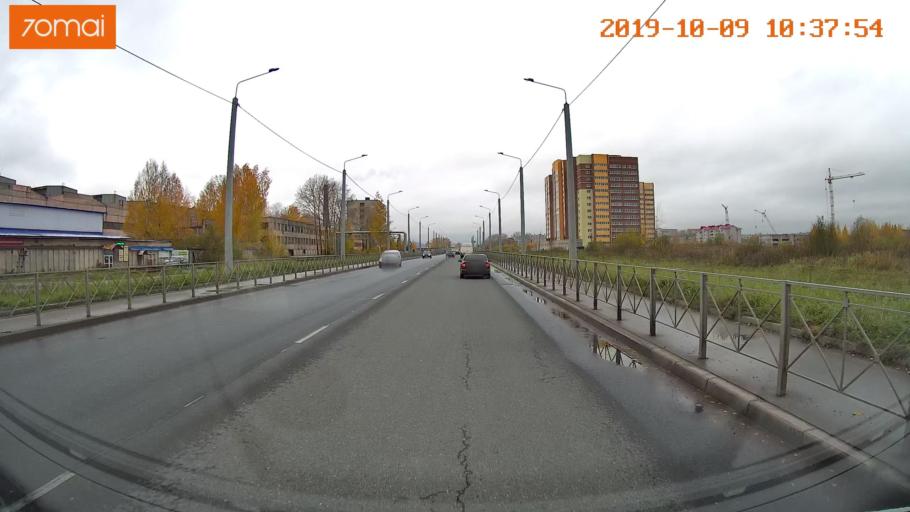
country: RU
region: Vologda
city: Vologda
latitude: 59.2357
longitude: 39.8541
